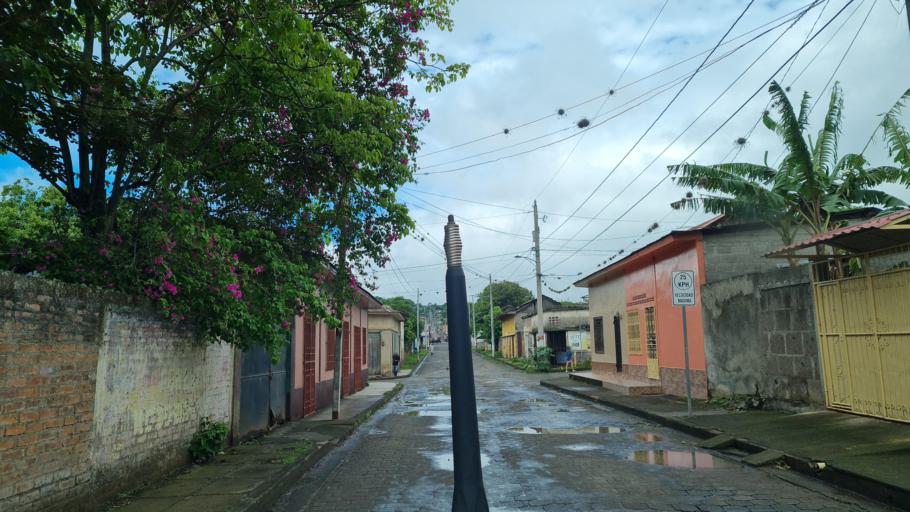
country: NI
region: Boaco
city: San Jose de los Remates
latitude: 12.6671
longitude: -85.7839
